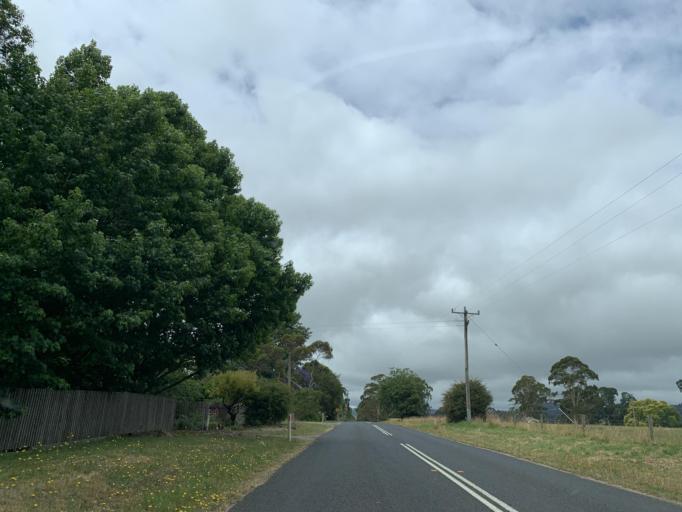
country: AU
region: Victoria
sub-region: Baw Baw
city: Warragul
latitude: -38.2412
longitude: 145.9450
